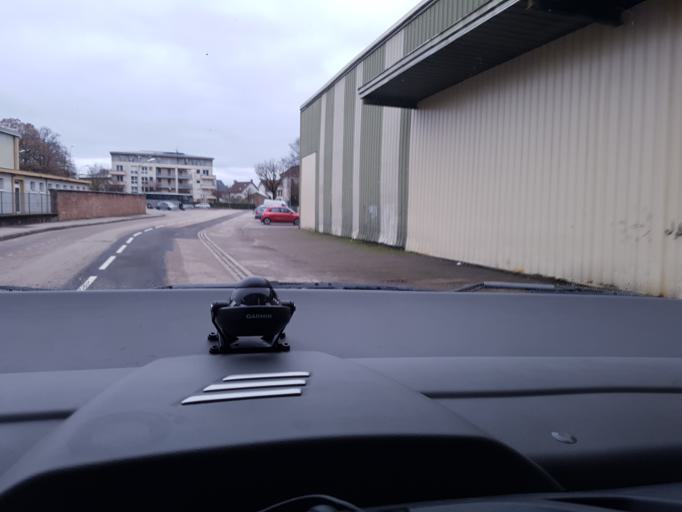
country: FR
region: Lorraine
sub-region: Departement des Vosges
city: Saint-Die-des-Vosges
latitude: 48.2864
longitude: 6.9547
